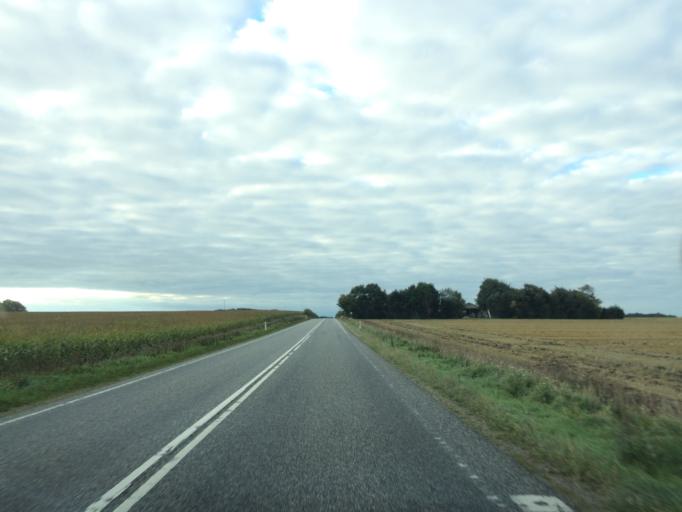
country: DK
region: Central Jutland
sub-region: Ringkobing-Skjern Kommune
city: Skjern
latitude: 55.9982
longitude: 8.5045
